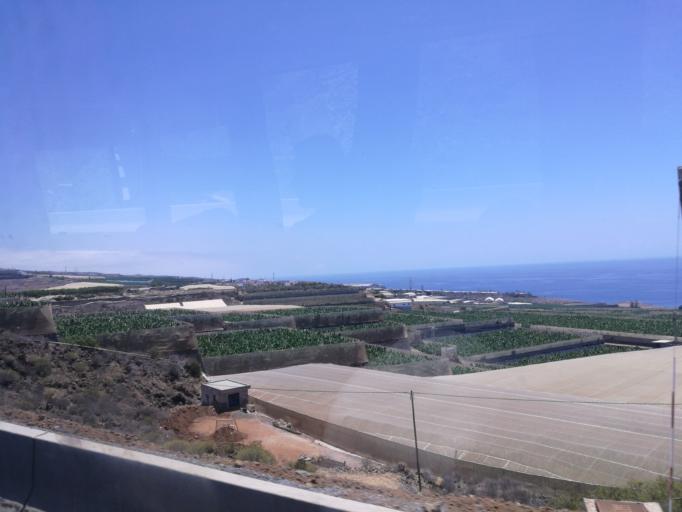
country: ES
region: Canary Islands
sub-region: Provincia de Santa Cruz de Tenerife
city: Guia de Isora
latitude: 28.1918
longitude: -16.8051
